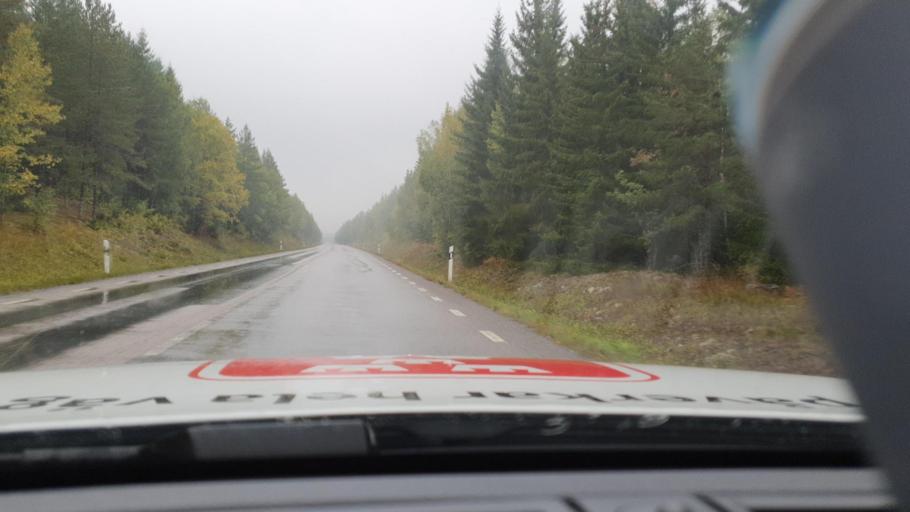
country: SE
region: Uppsala
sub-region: Tierps Kommun
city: Orbyhus
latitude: 60.2269
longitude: 17.6800
